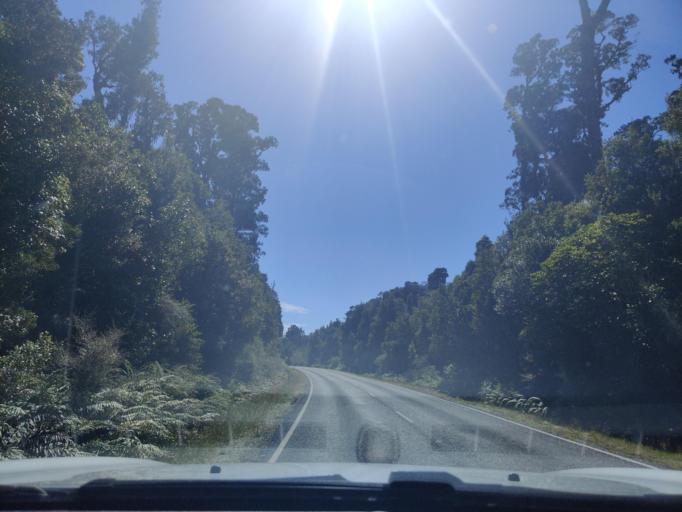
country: NZ
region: Otago
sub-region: Queenstown-Lakes District
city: Wanaka
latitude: -43.8310
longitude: 169.0635
